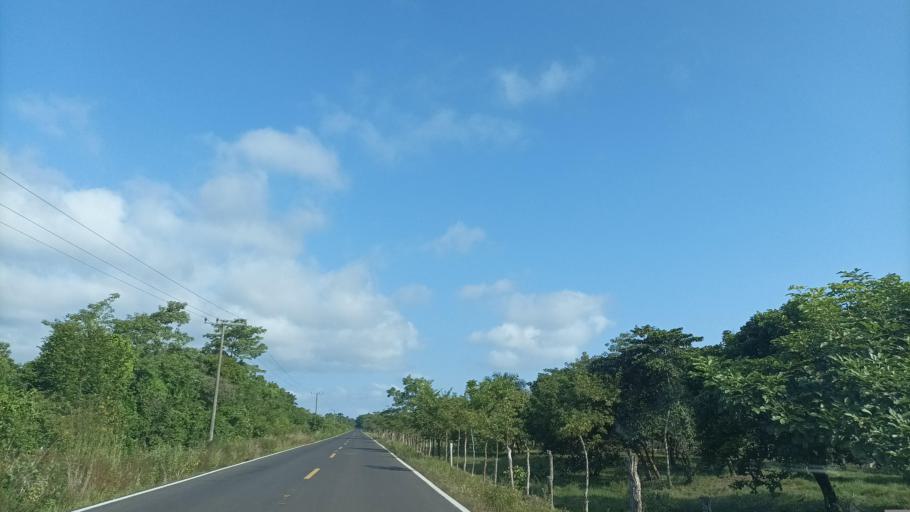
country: MX
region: Veracruz
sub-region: Chinameca
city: Chacalapa
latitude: 18.1578
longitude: -94.6575
